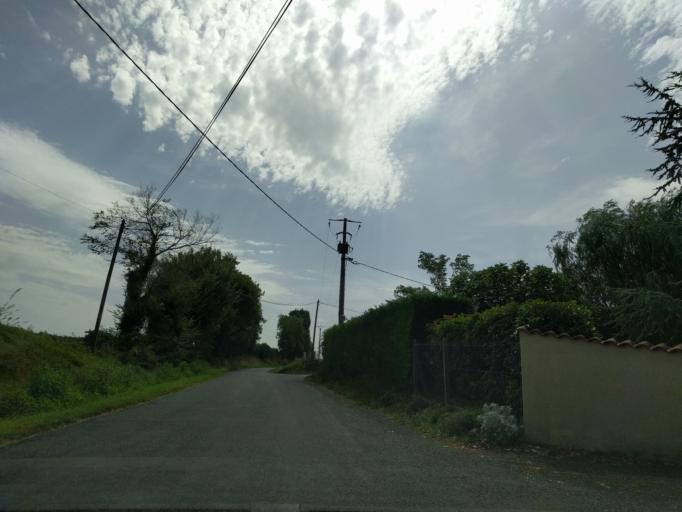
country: FR
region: Midi-Pyrenees
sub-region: Departement du Tarn
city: Castres
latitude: 43.6410
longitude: 2.2070
